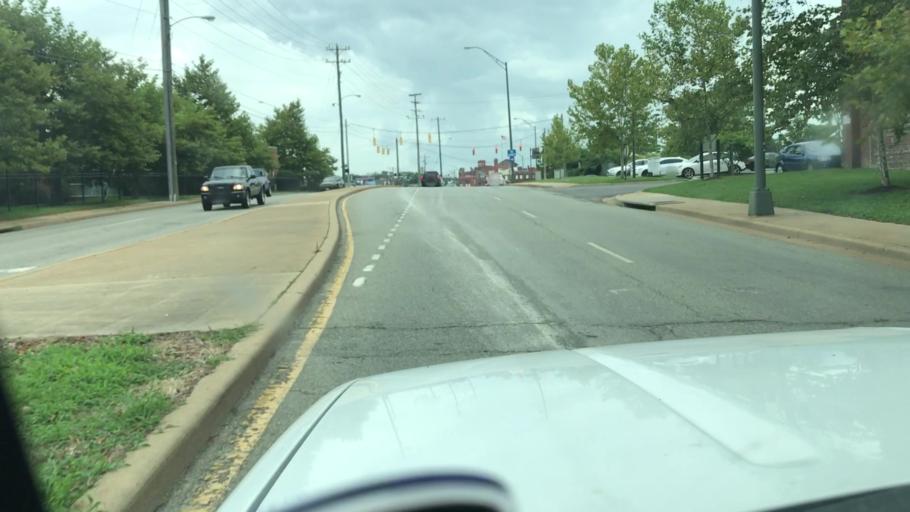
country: US
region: Virginia
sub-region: City of Richmond
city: Richmond
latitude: 37.5621
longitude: -77.4604
